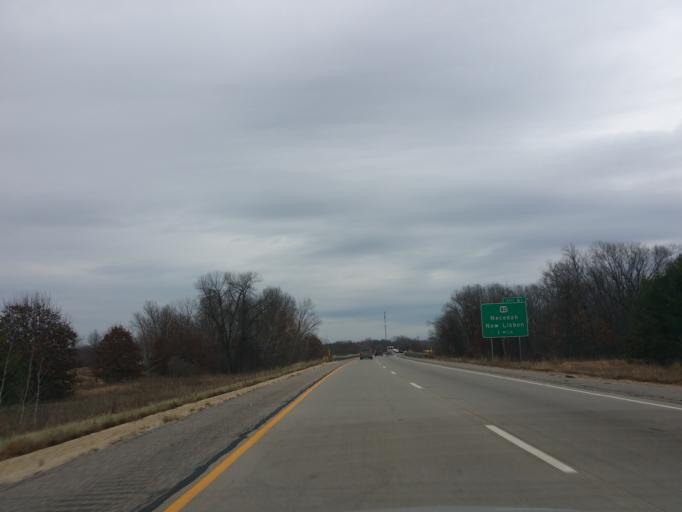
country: US
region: Wisconsin
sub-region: Juneau County
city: New Lisbon
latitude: 43.8935
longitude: -90.1695
